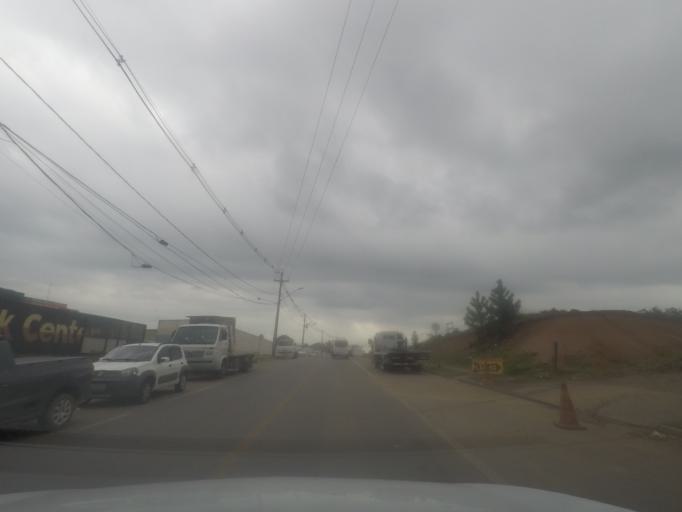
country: BR
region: Parana
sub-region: Sao Jose Dos Pinhais
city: Sao Jose dos Pinhais
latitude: -25.5609
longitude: -49.2646
